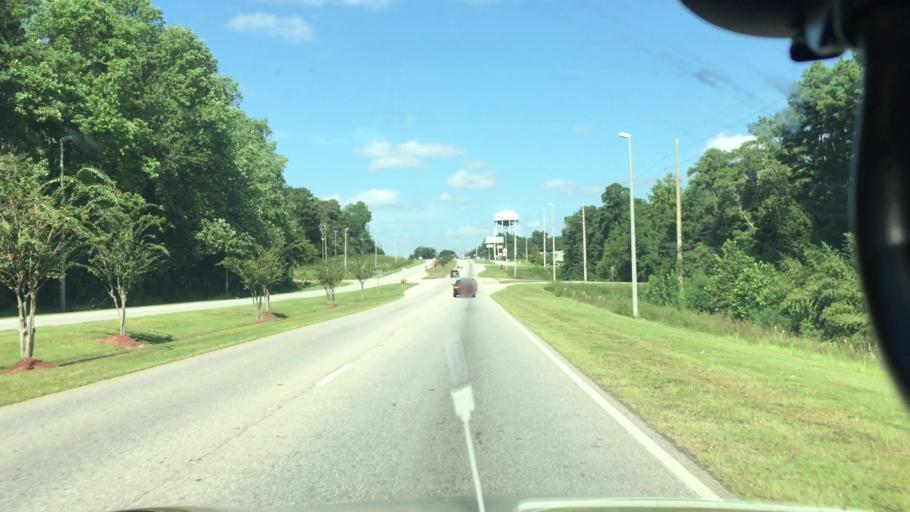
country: US
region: Alabama
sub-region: Coffee County
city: Enterprise
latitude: 31.3315
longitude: -85.8433
